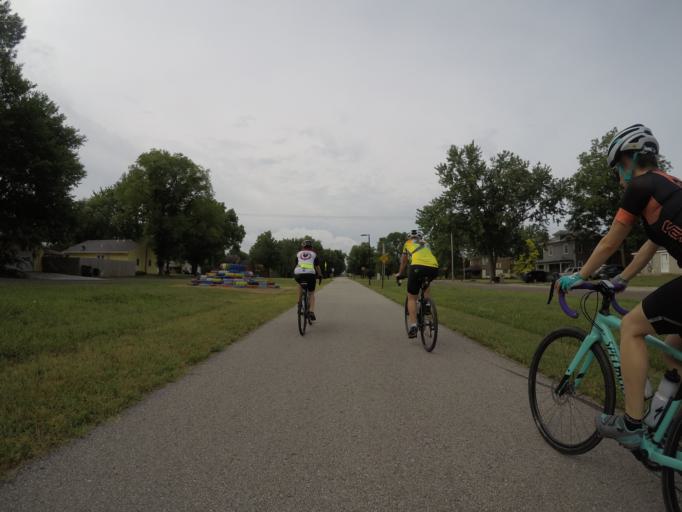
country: US
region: Kansas
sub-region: Franklin County
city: Ottawa
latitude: 38.6016
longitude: -95.2702
